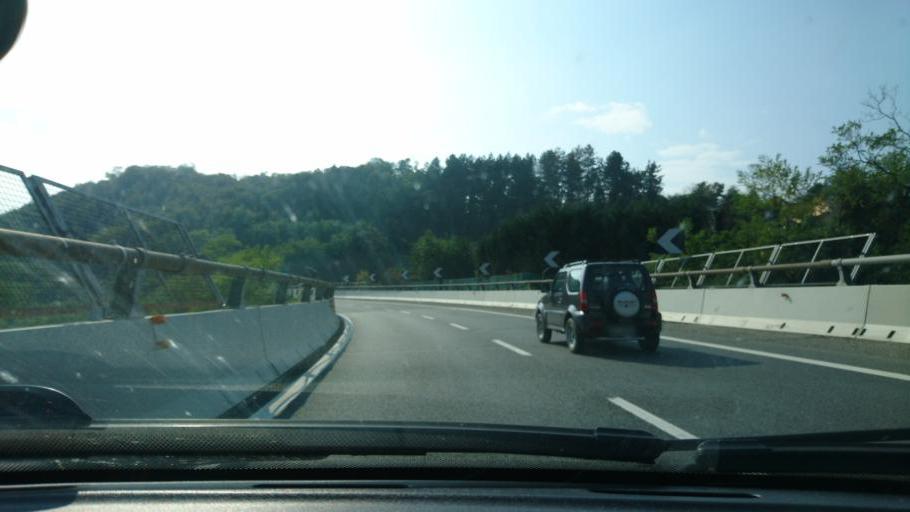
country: IT
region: Liguria
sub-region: Provincia di Savona
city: Altare
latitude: 44.3386
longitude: 8.3276
